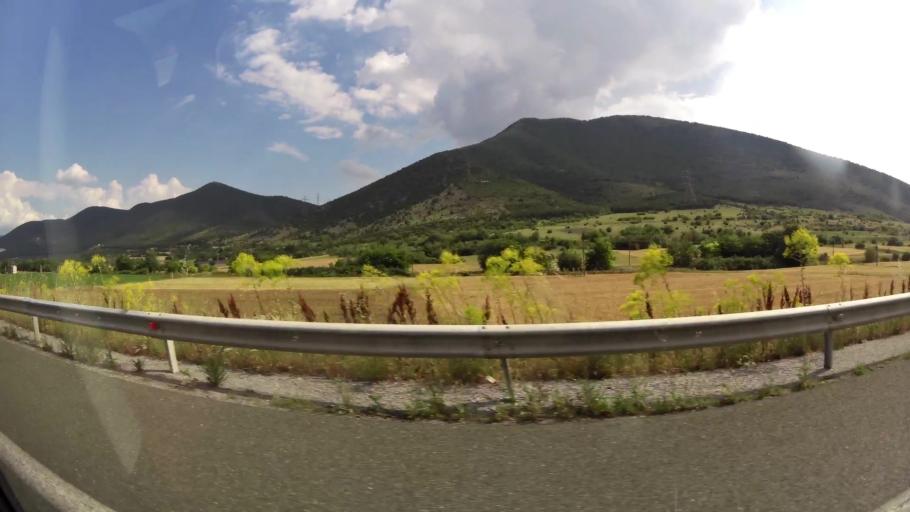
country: GR
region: West Macedonia
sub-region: Nomos Kozanis
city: Akrini
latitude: 40.3684
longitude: 21.9031
